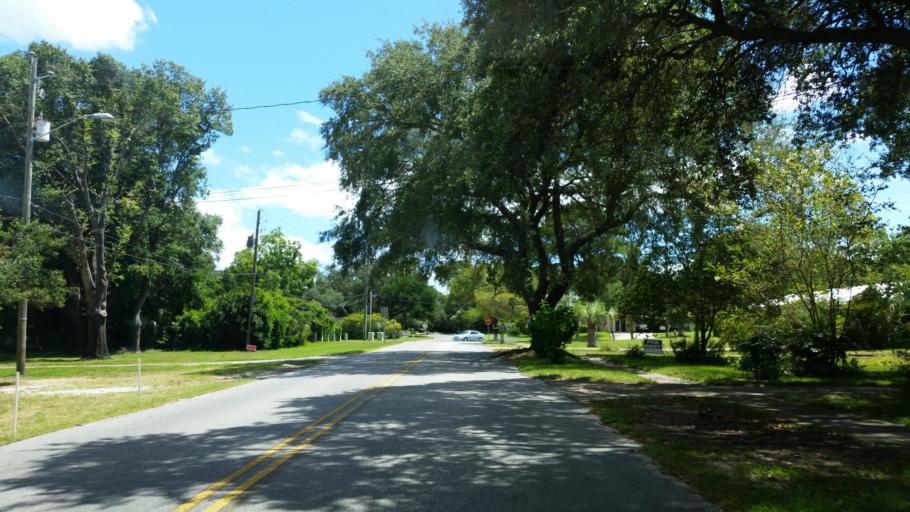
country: US
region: Florida
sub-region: Okaloosa County
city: Ocean City
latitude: 30.4238
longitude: -86.5941
